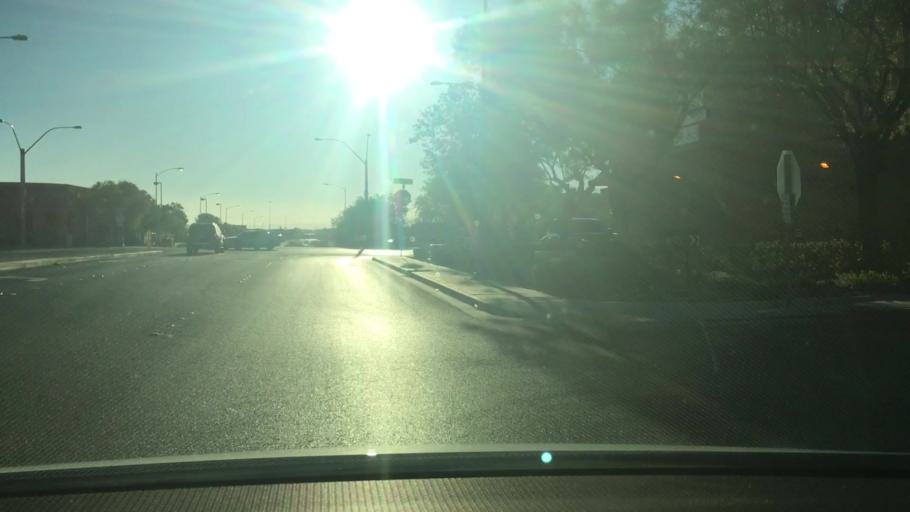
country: US
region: Nevada
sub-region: Clark County
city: Summerlin South
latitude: 36.0776
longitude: -115.2984
